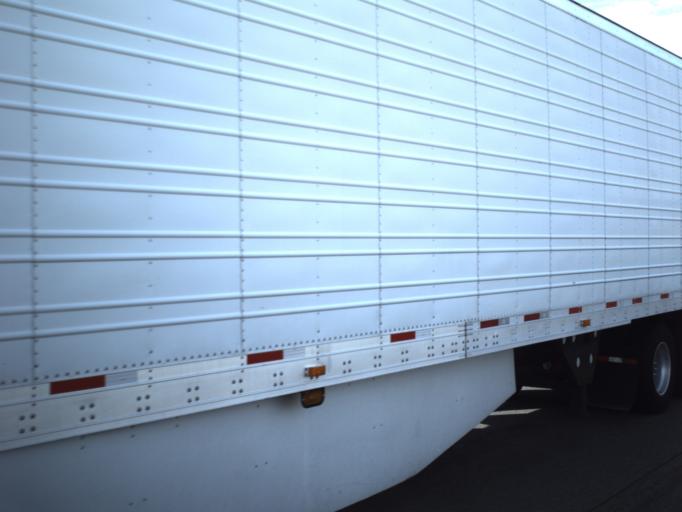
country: US
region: Utah
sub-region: Tooele County
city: Grantsville
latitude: 40.7592
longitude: -113.0163
